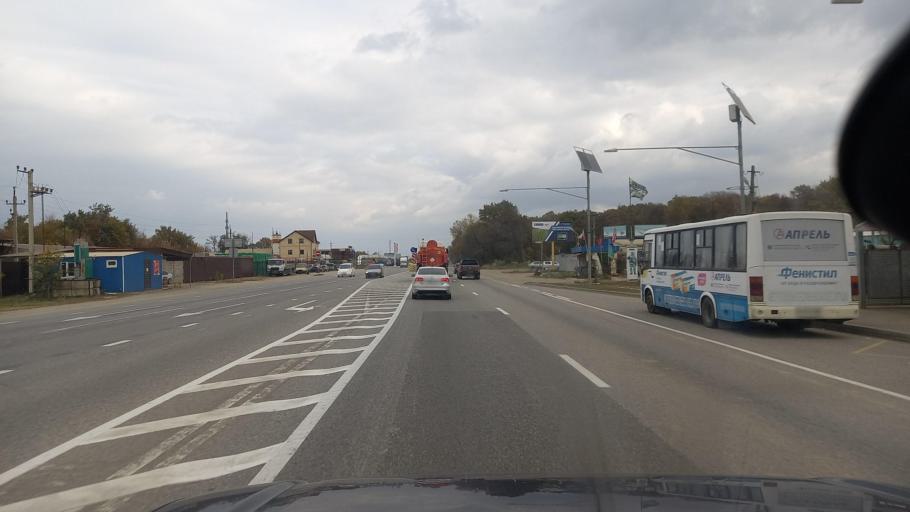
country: RU
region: Krasnodarskiy
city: Afipskiy
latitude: 44.9037
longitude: 38.8741
